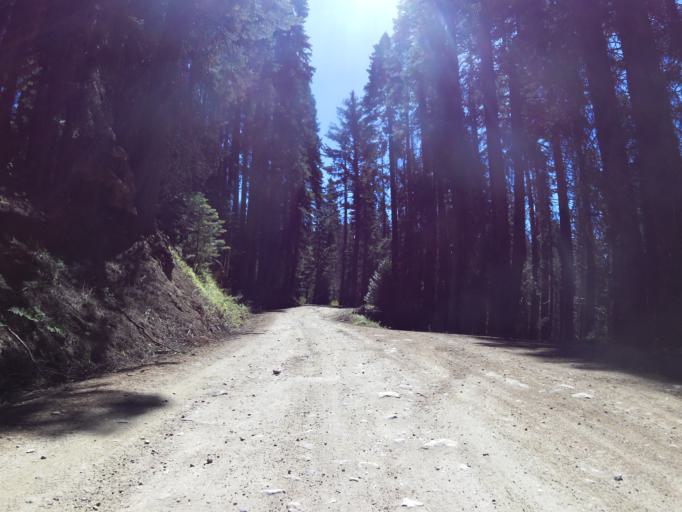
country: US
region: California
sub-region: Madera County
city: Oakhurst
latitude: 37.4443
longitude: -119.5193
